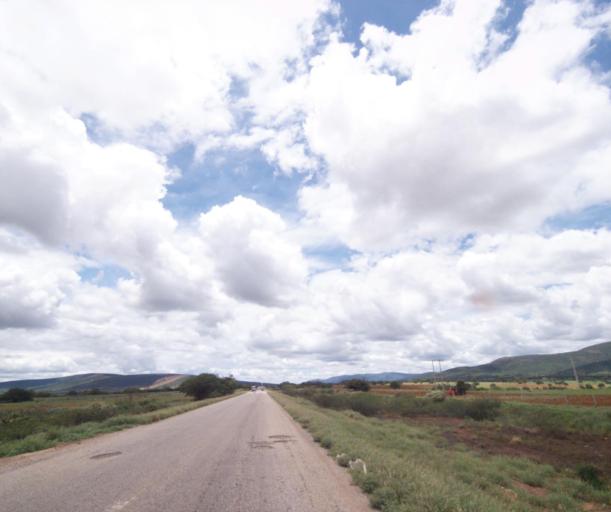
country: BR
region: Bahia
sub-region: Brumado
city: Brumado
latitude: -14.1596
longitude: -41.5263
